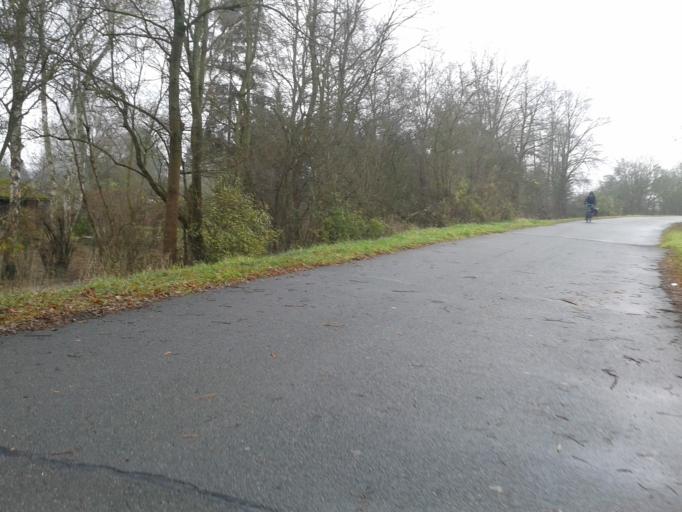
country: DE
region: Bavaria
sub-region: Upper Franconia
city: Hallstadt
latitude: 49.9189
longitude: 10.8771
